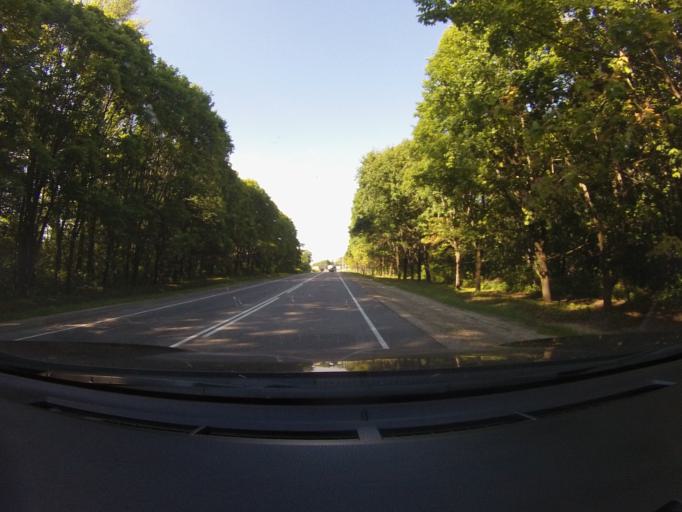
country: RU
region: Tula
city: Bol'shoye Skuratovo
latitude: 53.3918
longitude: 36.7512
